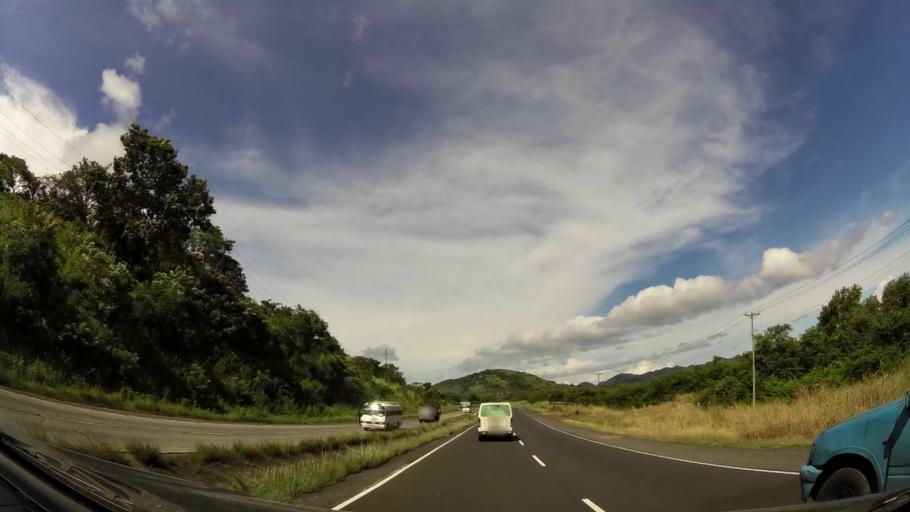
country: PA
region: Panama
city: Bejuco
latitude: 8.6547
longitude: -79.8716
